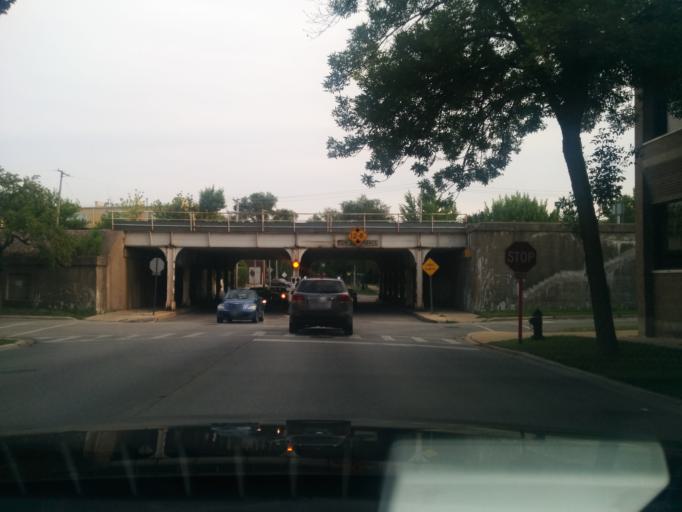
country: US
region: Illinois
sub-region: Cook County
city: Forest Park
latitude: 41.8873
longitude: -87.8148
